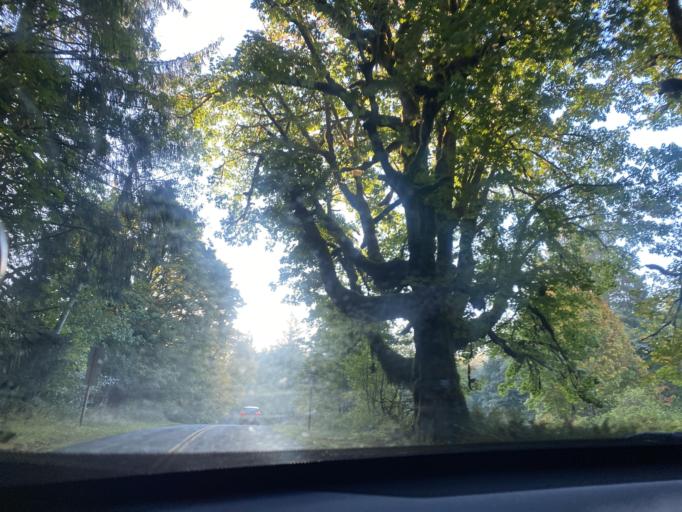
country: US
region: Washington
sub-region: Clallam County
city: Forks
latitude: 47.8168
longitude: -124.1509
